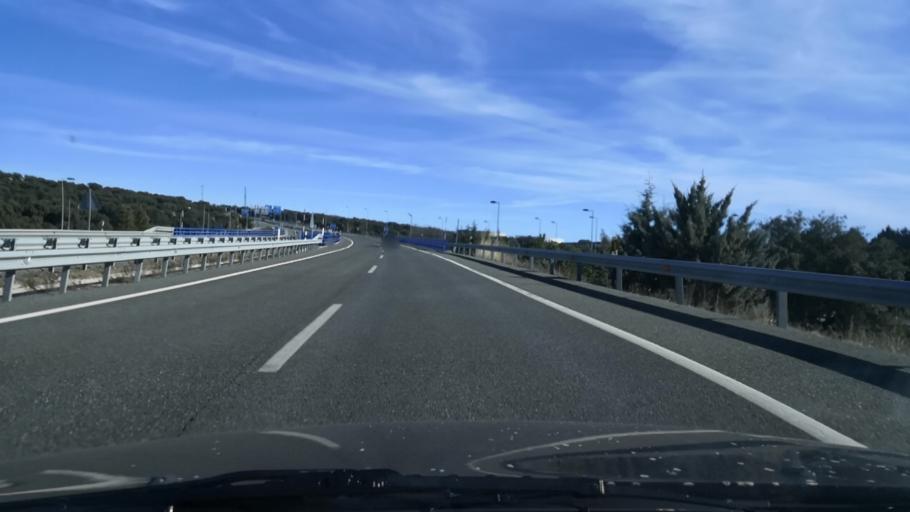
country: ES
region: Castille and Leon
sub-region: Provincia de Avila
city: Avila
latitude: 40.6710
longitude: -4.6524
